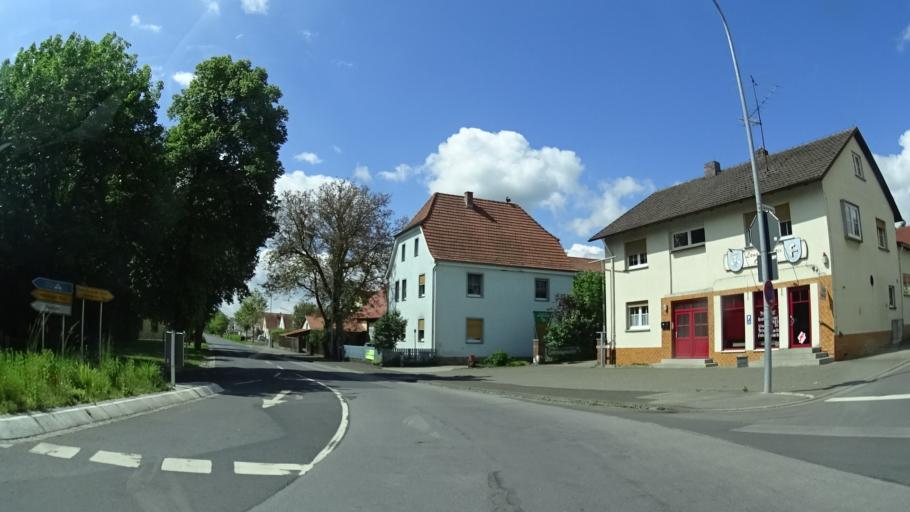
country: DE
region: Bavaria
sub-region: Regierungsbezirk Unterfranken
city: Mellrichstadt
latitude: 50.4259
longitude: 10.2972
